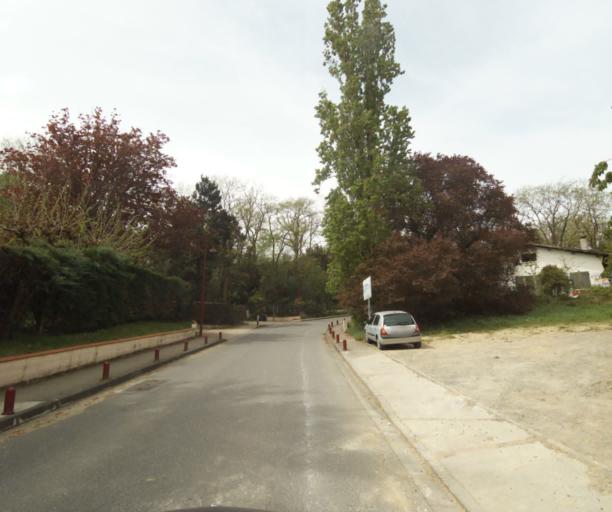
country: FR
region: Midi-Pyrenees
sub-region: Departement de la Haute-Garonne
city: Pechabou
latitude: 43.4998
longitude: 1.5061
